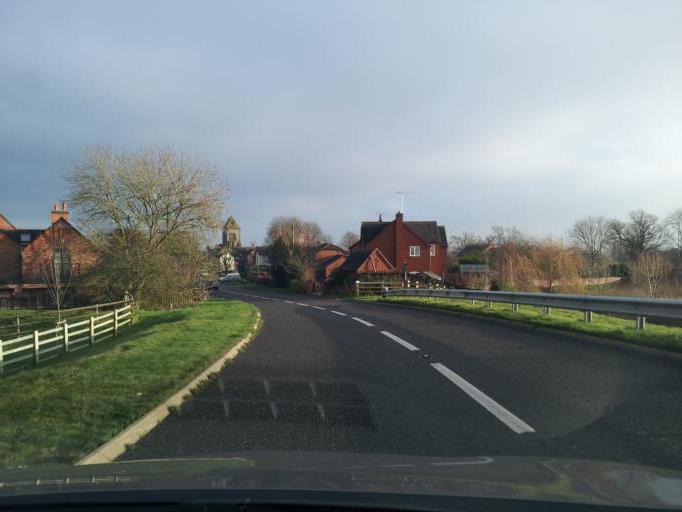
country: GB
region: England
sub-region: Derbyshire
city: Rodsley
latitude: 52.8695
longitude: -1.7189
